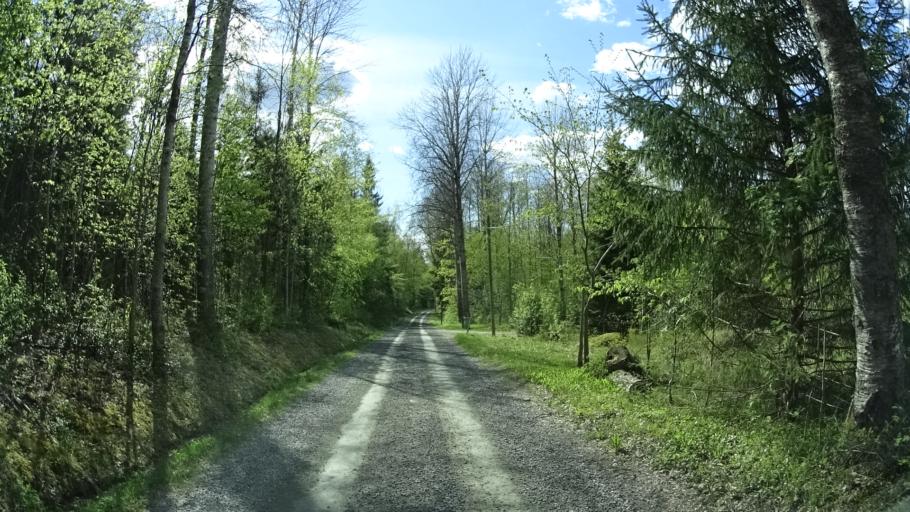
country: SE
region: OErebro
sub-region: Nora Kommun
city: As
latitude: 59.4426
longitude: 14.8323
